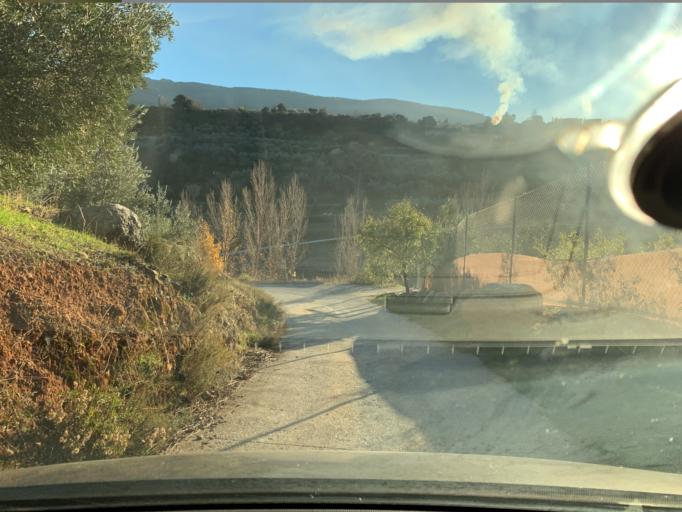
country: ES
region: Andalusia
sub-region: Provincia de Granada
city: Dilar
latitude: 37.0749
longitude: -3.5920
